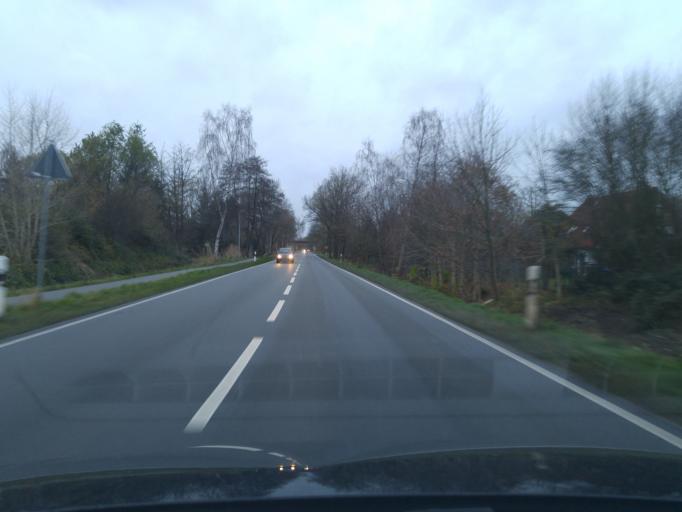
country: DE
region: Schleswig-Holstein
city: Lauenburg
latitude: 53.3608
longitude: 10.5609
